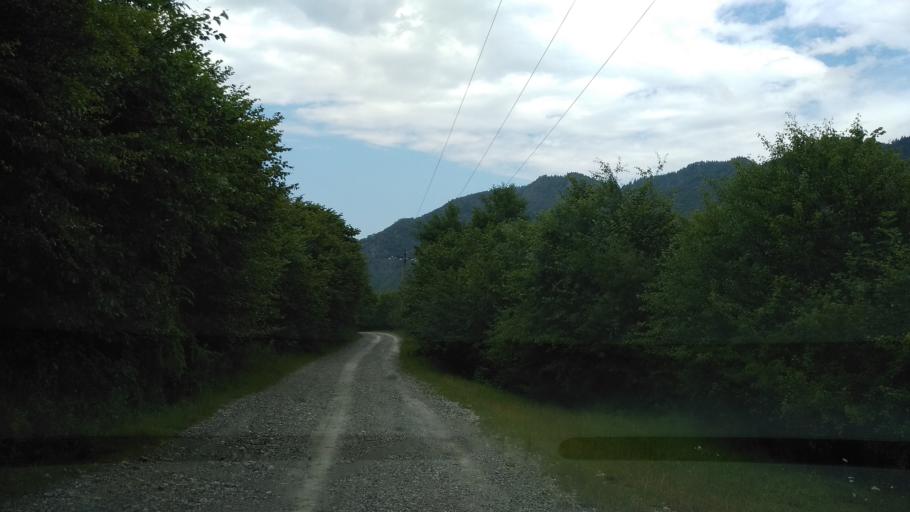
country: RO
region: Hunedoara
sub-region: Comuna Rau de Mori
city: Rau de Mori
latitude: 45.4498
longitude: 22.8955
